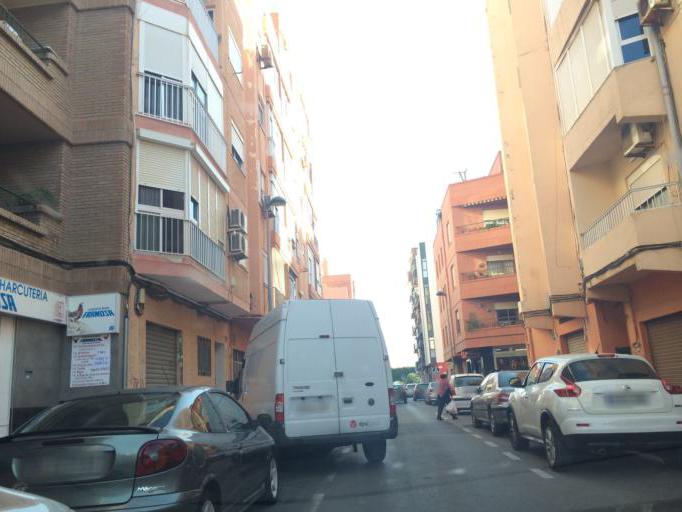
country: ES
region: Andalusia
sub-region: Provincia de Almeria
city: Almeria
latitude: 36.8275
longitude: -2.4470
